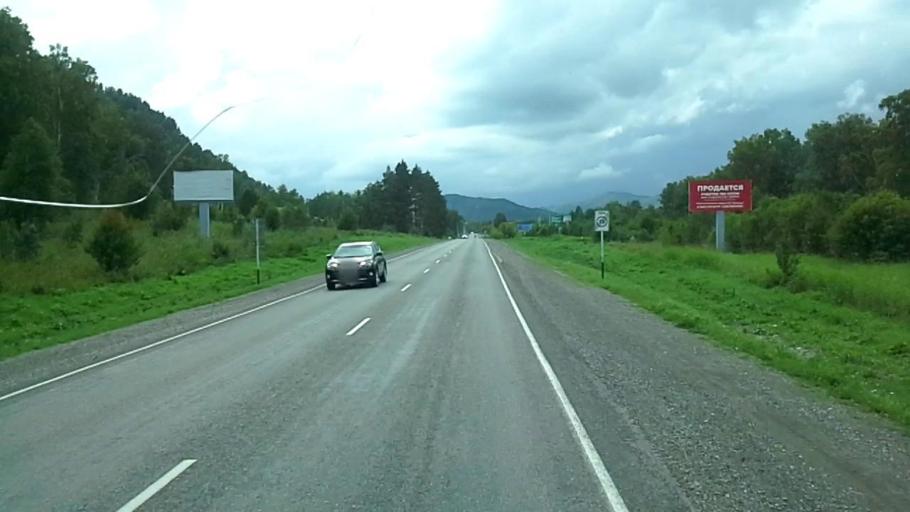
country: RU
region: Altay
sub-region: Mayminskiy Rayon
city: Manzherok
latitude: 51.8723
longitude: 85.7937
